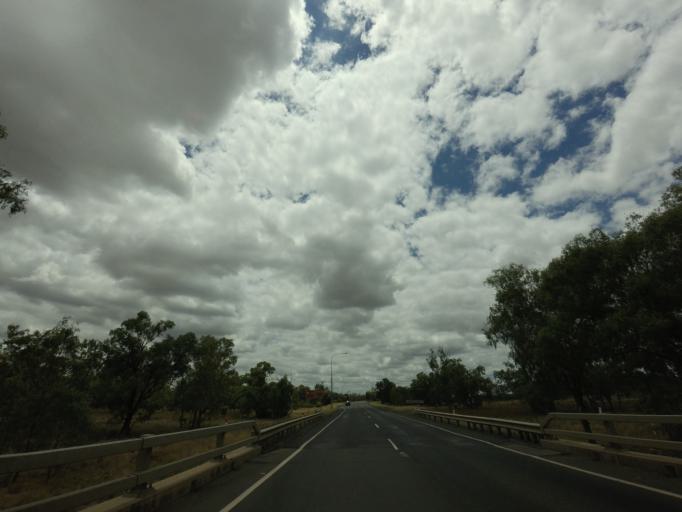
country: AU
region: Queensland
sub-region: Goondiwindi
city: Goondiwindi
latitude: -28.3970
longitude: 150.3126
